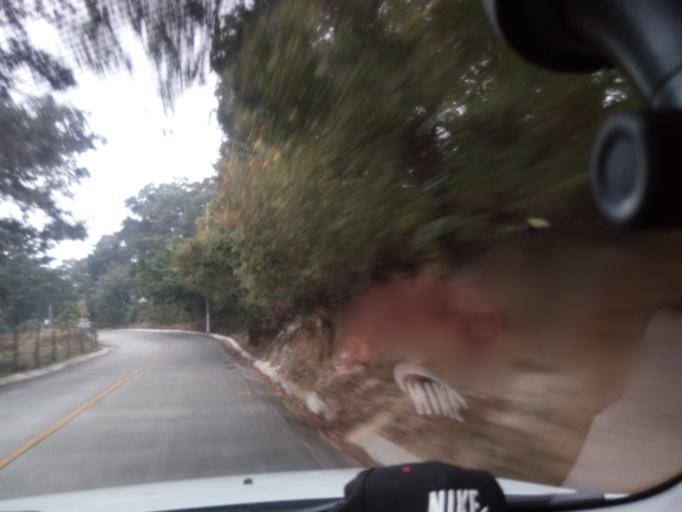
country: GT
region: Sacatepequez
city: Santa Lucia Milpas Altas
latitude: 14.5877
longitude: -90.7094
